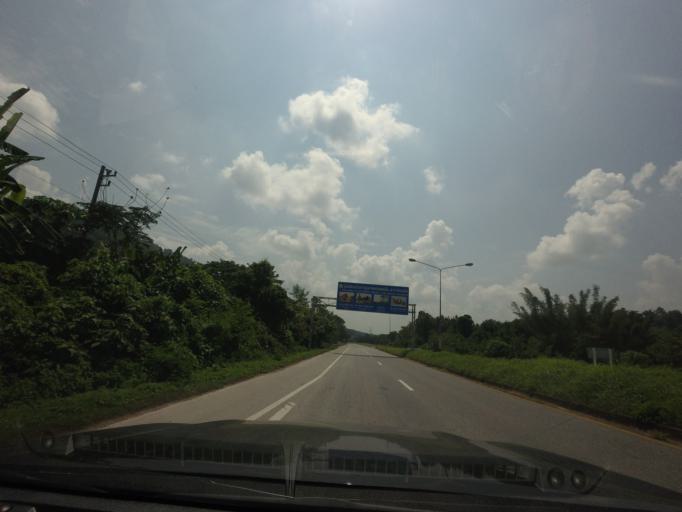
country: TH
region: Uttaradit
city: Lap Lae
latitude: 17.7945
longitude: 100.1165
